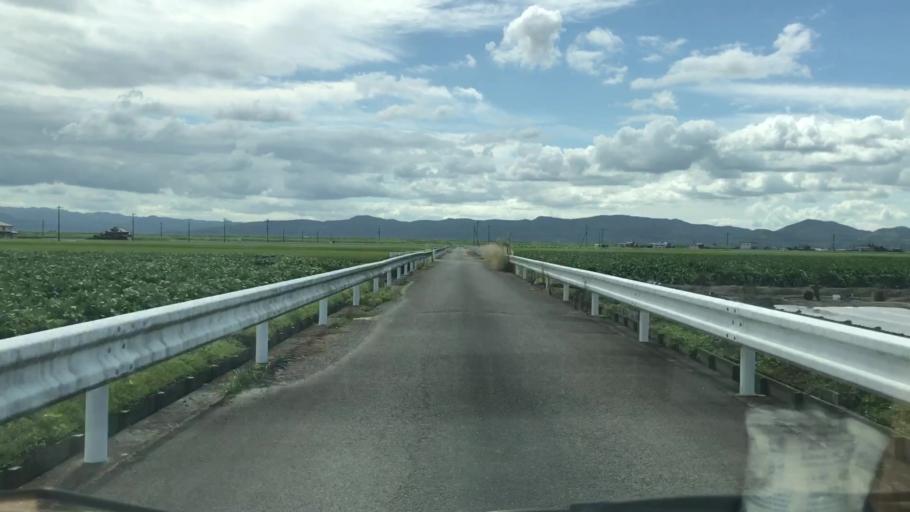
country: JP
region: Saga Prefecture
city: Saga-shi
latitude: 33.2079
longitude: 130.1818
